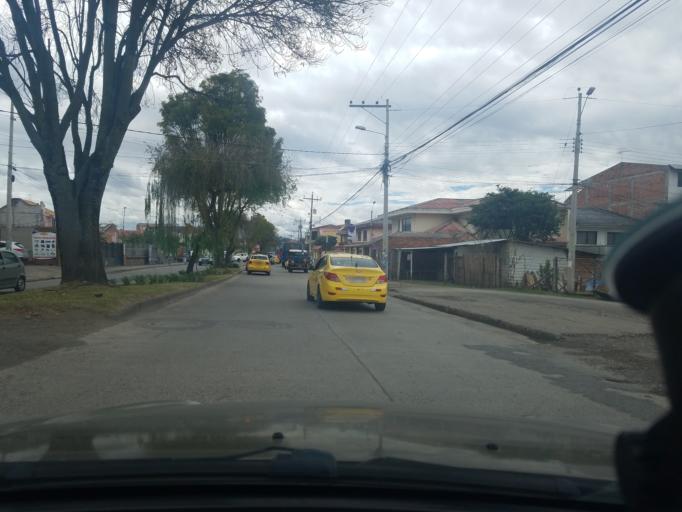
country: EC
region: Azuay
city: Cuenca
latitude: -2.9149
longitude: -79.0322
